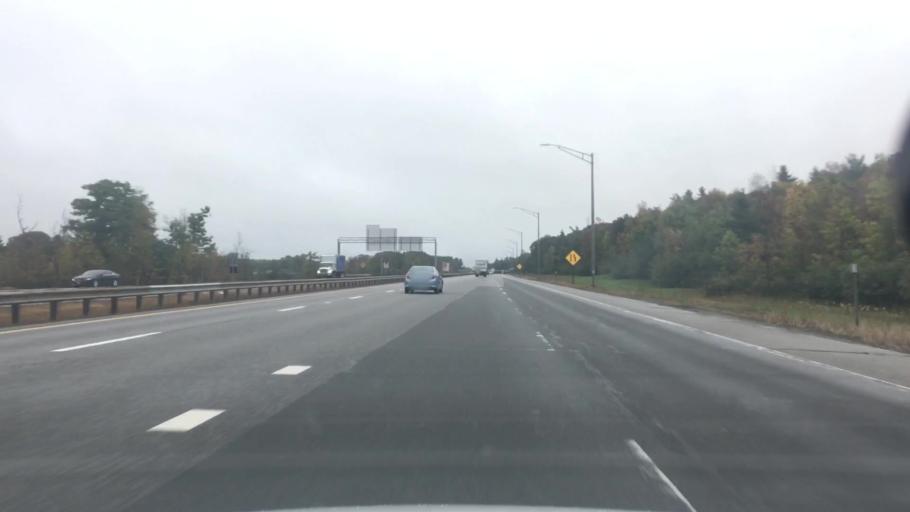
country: US
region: Maine
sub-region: Kennebec County
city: Gardiner
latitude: 44.2235
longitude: -69.8184
